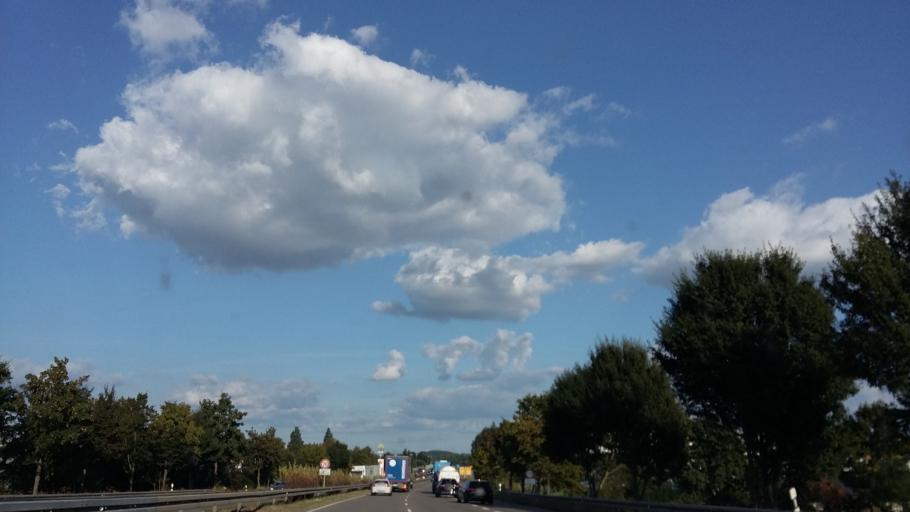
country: DE
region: Bavaria
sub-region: Swabia
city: Neu-Ulm
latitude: 48.3871
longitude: 10.0295
